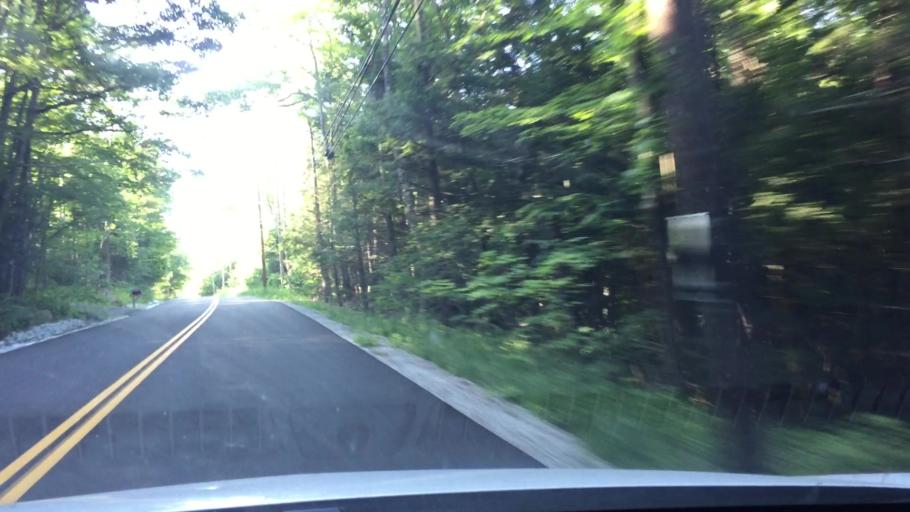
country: US
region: Massachusetts
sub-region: Berkshire County
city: Lee
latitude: 42.2830
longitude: -73.2122
